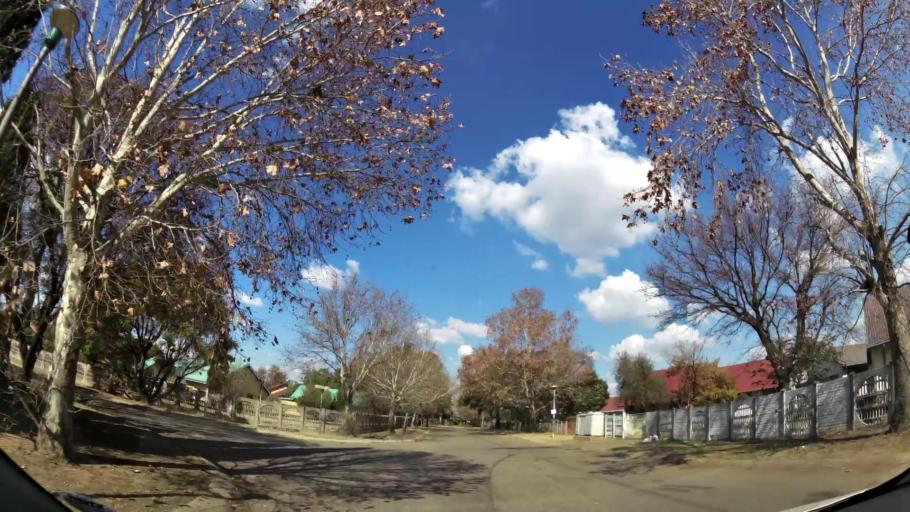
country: ZA
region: Mpumalanga
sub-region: Nkangala District Municipality
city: Witbank
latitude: -25.9465
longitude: 29.2466
